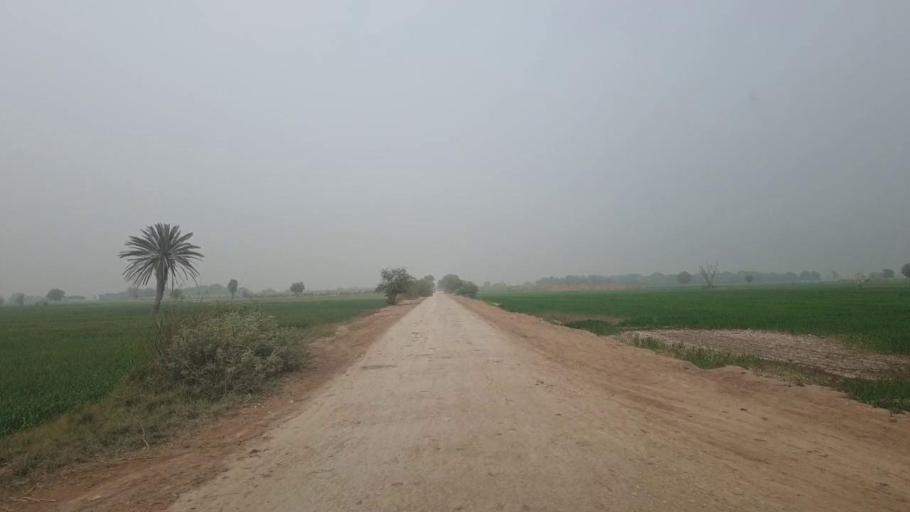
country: PK
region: Sindh
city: Tando Adam
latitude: 25.7592
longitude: 68.7026
